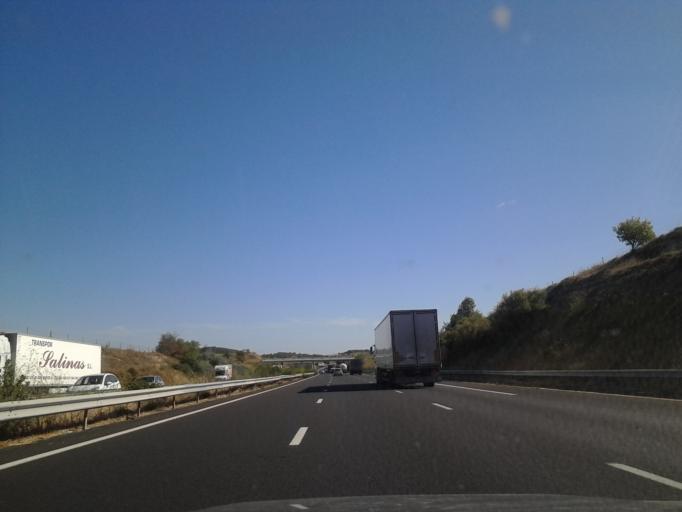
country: FR
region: Languedoc-Roussillon
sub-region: Departement de l'Herault
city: Lespignan
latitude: 43.2738
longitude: 3.1822
